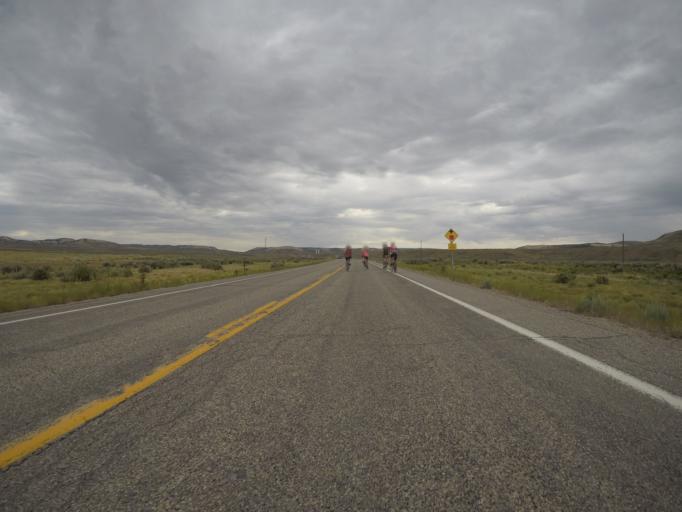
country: US
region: Wyoming
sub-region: Lincoln County
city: Kemmerer
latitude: 41.8171
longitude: -110.7217
